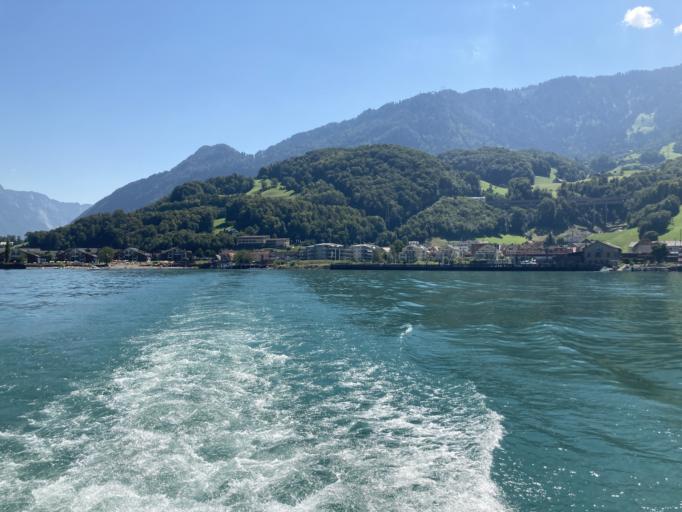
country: CH
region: Saint Gallen
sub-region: Wahlkreis Sarganserland
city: Quarten
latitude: 47.1165
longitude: 9.2490
